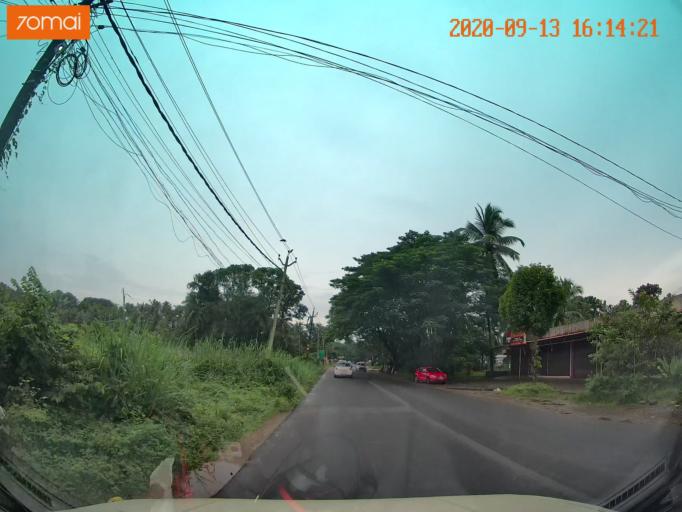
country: IN
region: Kerala
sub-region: Kottayam
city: Palackattumala
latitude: 9.6891
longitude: 76.6344
